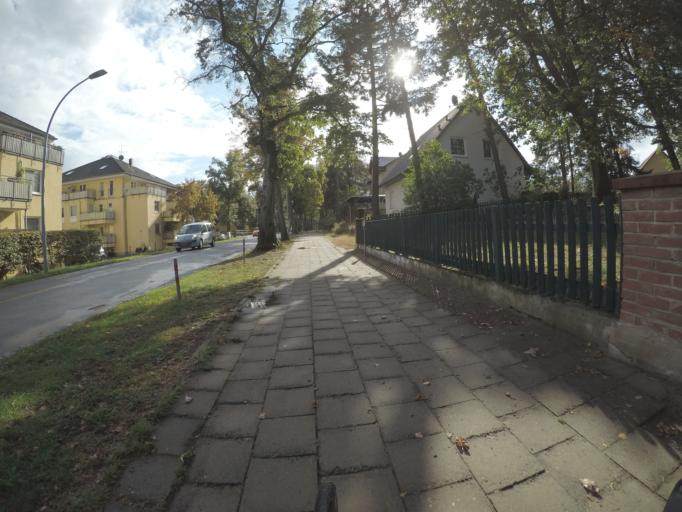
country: DE
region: Brandenburg
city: Strausberg
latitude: 52.5408
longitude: 13.8540
